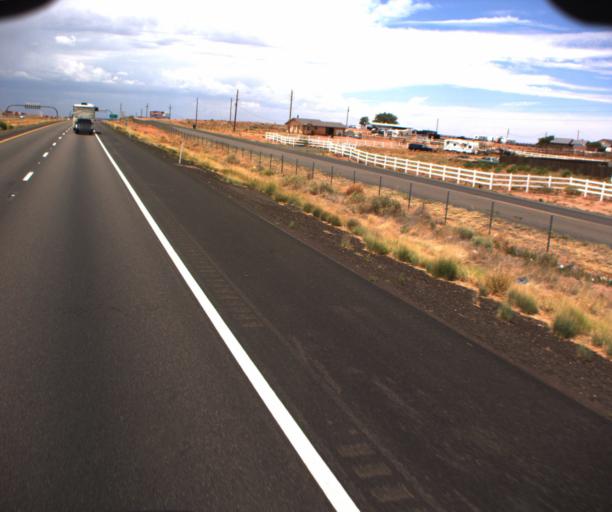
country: US
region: Arizona
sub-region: Coconino County
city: LeChee
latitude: 35.0406
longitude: -110.7421
